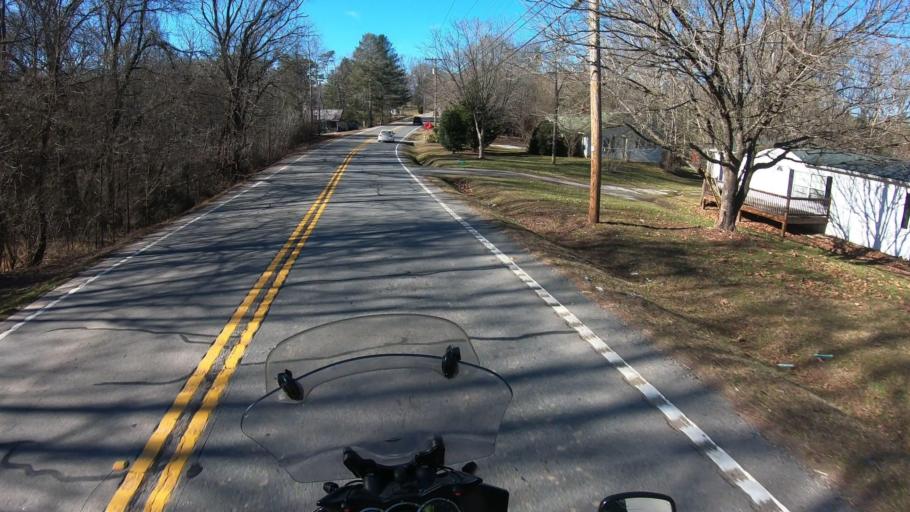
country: US
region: Georgia
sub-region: Fannin County
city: Blue Ridge
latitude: 34.9262
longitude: -84.2877
